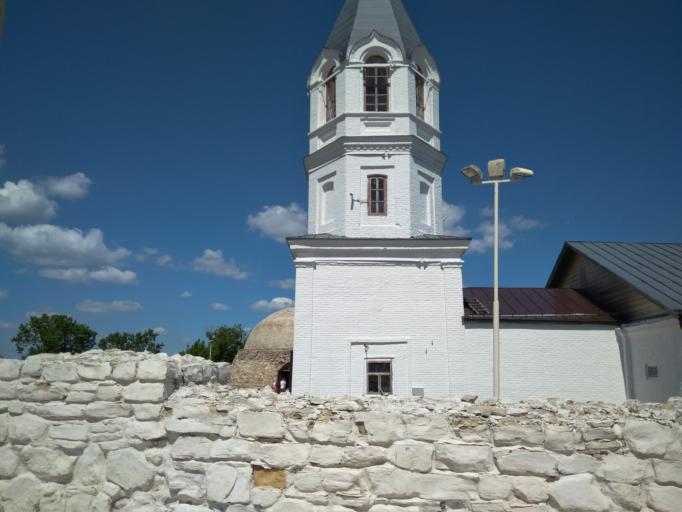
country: RU
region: Tatarstan
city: Bolgar
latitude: 54.9857
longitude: 49.0561
